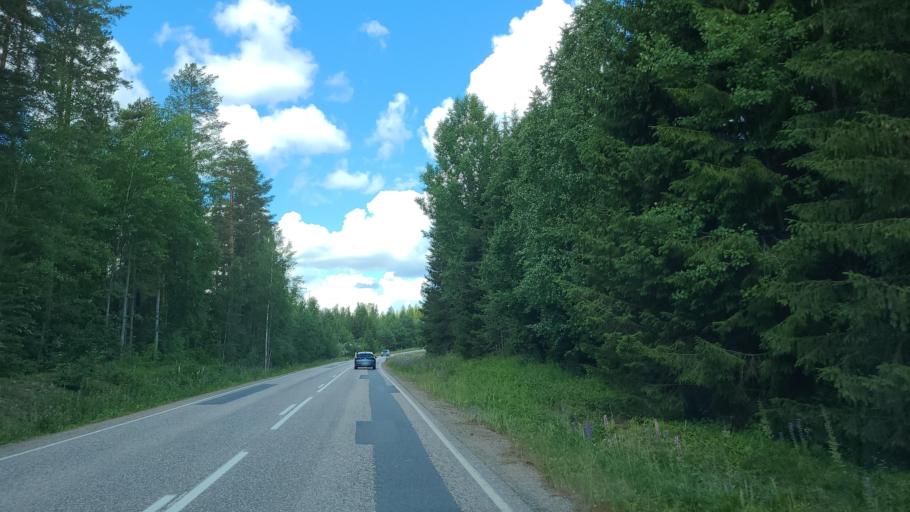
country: FI
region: Northern Savo
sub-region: Koillis-Savo
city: Kaavi
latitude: 62.9122
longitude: 28.7070
